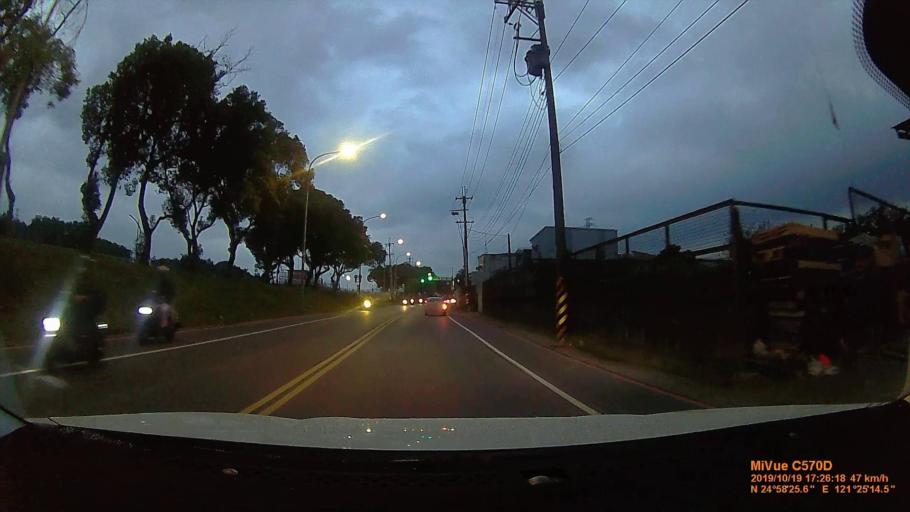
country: TW
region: Taipei
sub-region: Taipei
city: Banqiao
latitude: 24.9736
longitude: 121.4205
